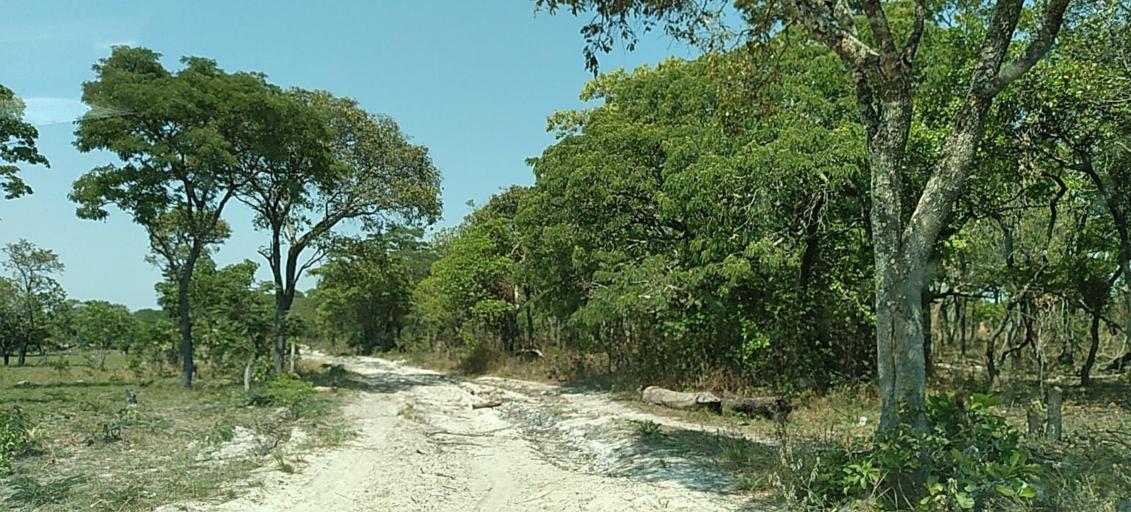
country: ZM
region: Copperbelt
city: Mpongwe
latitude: -13.7800
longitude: 28.1067
